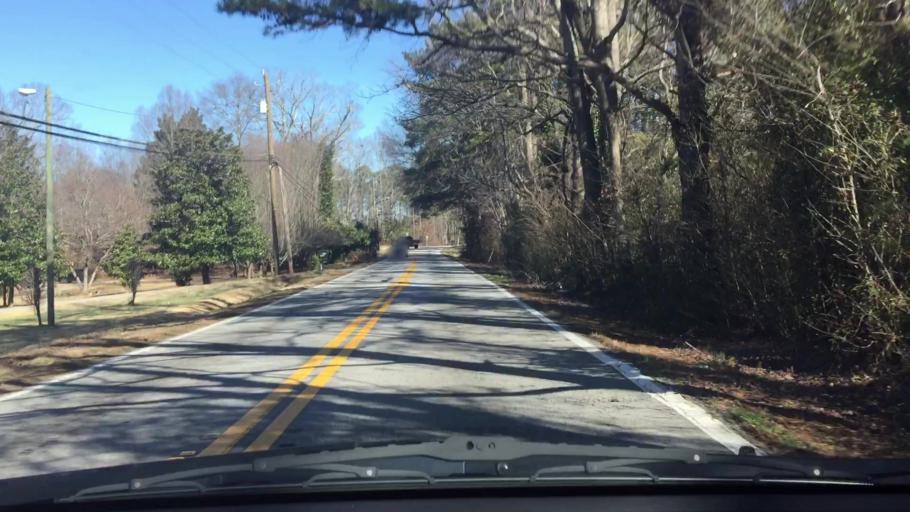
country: US
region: Georgia
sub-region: Clayton County
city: Conley
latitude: 33.6383
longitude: -84.2828
